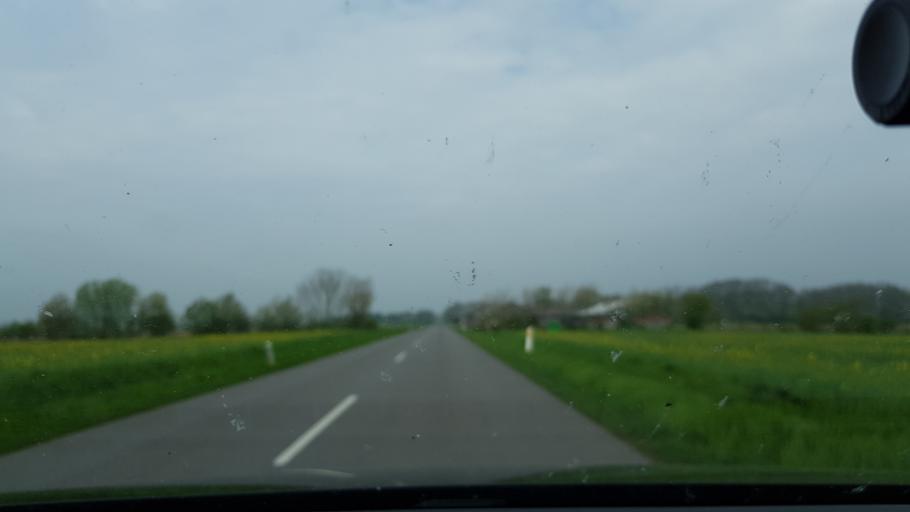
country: DK
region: Capital Region
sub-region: Bornholm Kommune
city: Nexo
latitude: 55.0126
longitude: 15.0959
